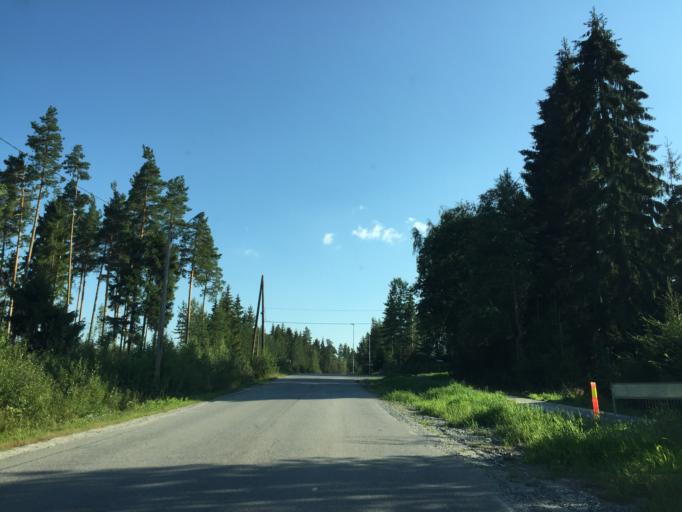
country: NO
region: Akershus
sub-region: Nes
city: Fjellfoten
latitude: 60.0912
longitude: 11.4782
